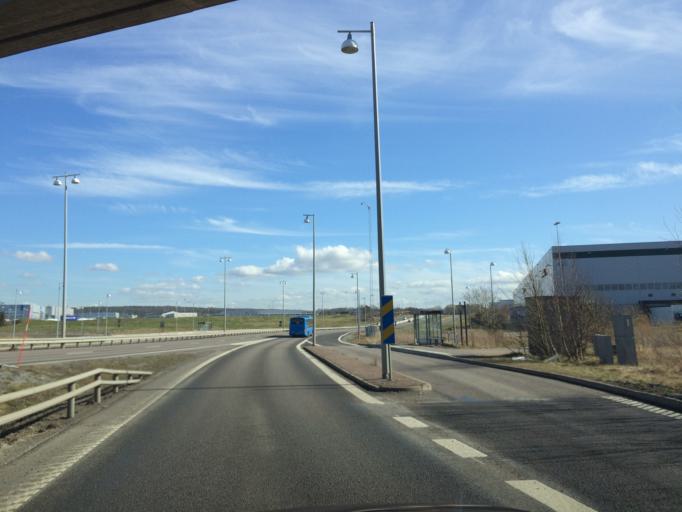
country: SE
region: Vaestra Goetaland
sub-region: Goteborg
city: Torslanda
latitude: 57.7178
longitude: 11.8184
